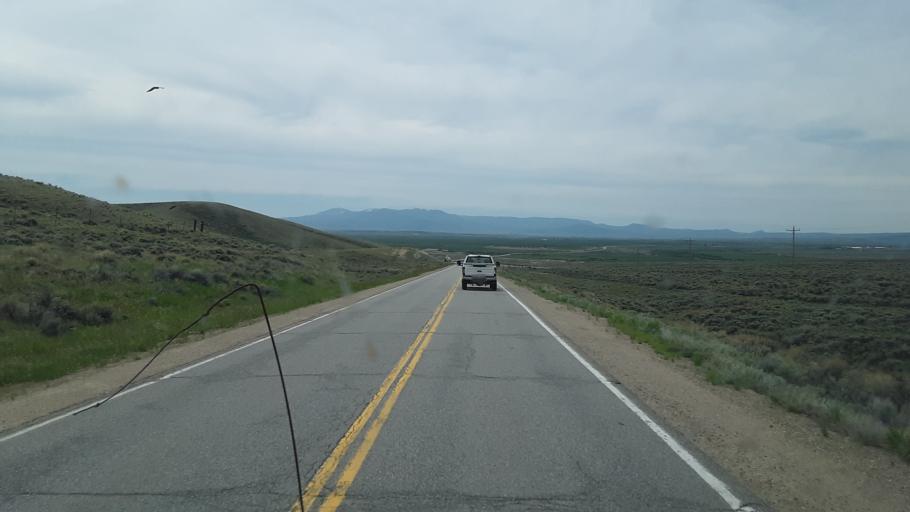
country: US
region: Colorado
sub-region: Jackson County
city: Walden
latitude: 40.6547
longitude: -106.3978
